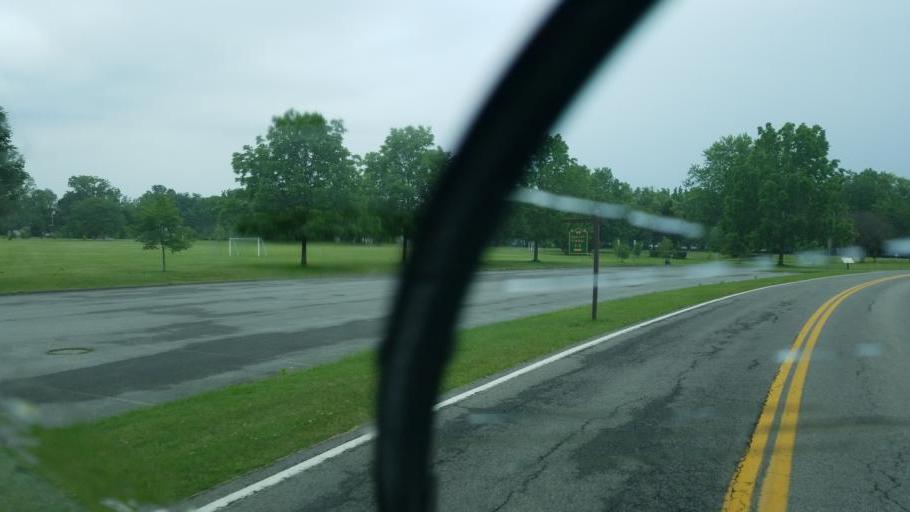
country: US
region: New York
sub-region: Niagara County
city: Youngstown
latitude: 43.2575
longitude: -79.0501
